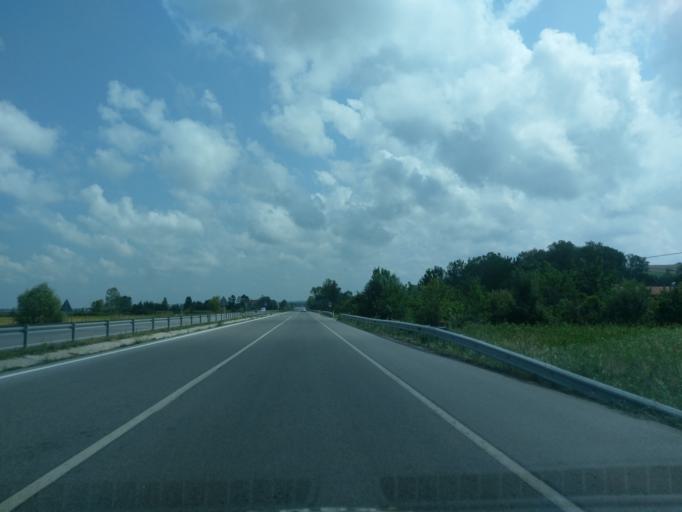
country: TR
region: Samsun
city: Alacam
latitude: 41.6114
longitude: 35.7146
